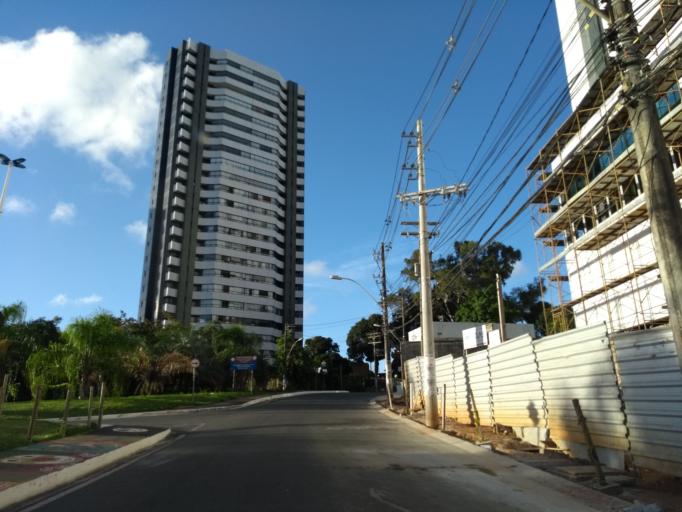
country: BR
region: Bahia
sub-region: Salvador
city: Salvador
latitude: -12.9979
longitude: -38.4885
